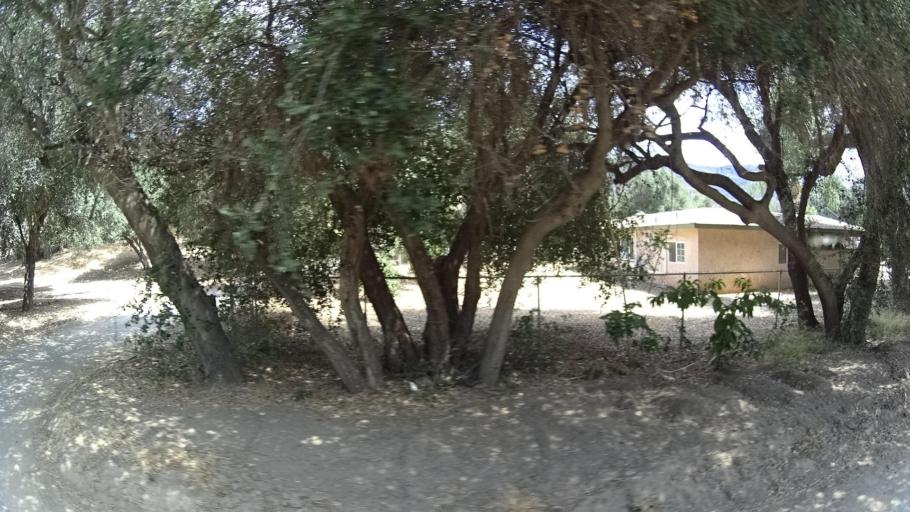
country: US
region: California
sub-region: San Diego County
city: Hidden Meadows
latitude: 33.1982
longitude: -117.0890
